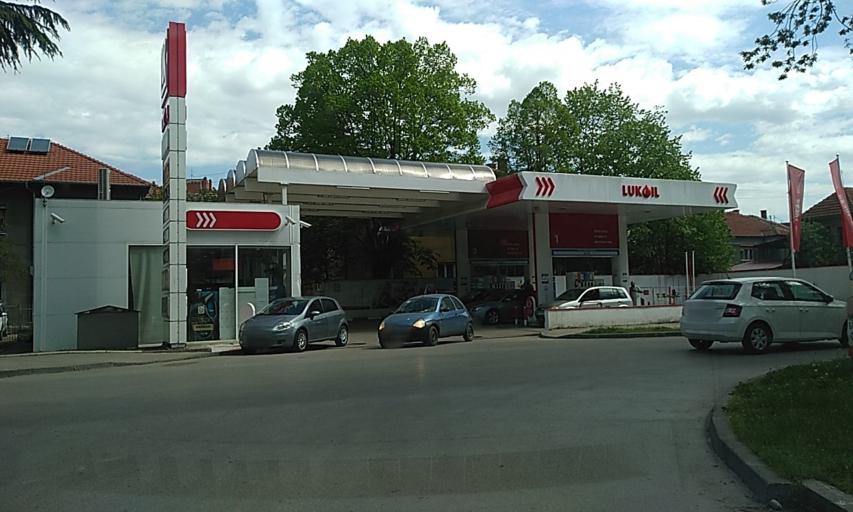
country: RS
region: Central Serbia
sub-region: Nisavski Okrug
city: Nis
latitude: 43.3190
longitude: 21.9142
